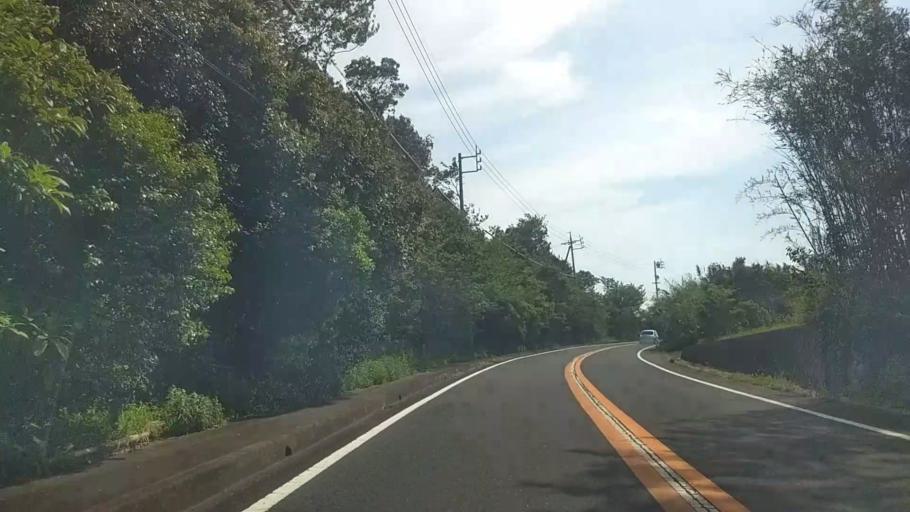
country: JP
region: Shizuoka
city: Kosai-shi
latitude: 34.7356
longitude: 137.5999
